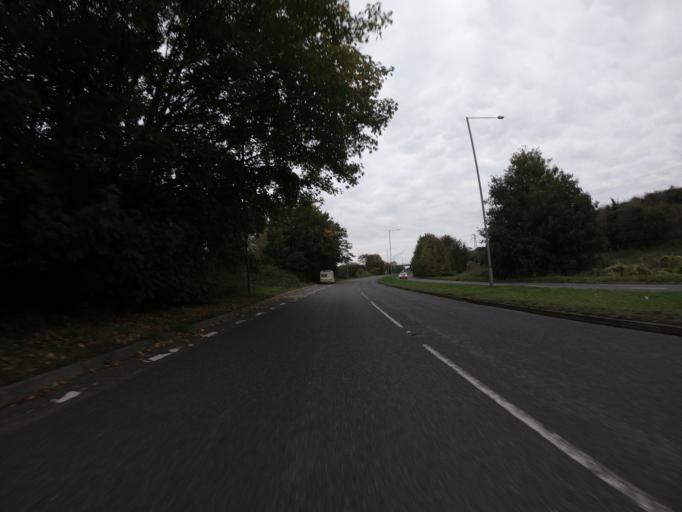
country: GB
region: England
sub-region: Borough of Thurrock
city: Chadwell St Mary
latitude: 51.4826
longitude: 0.3480
